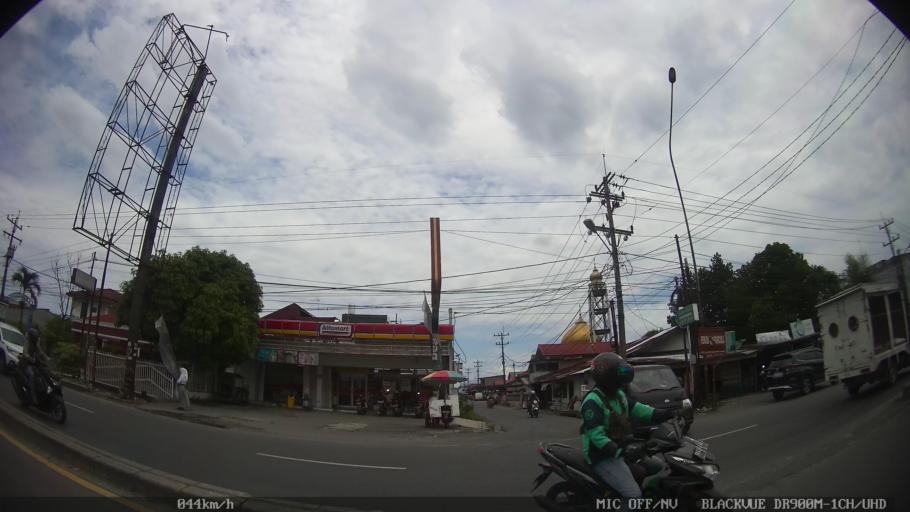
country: ID
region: North Sumatra
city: Sunggal
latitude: 3.5983
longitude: 98.5917
